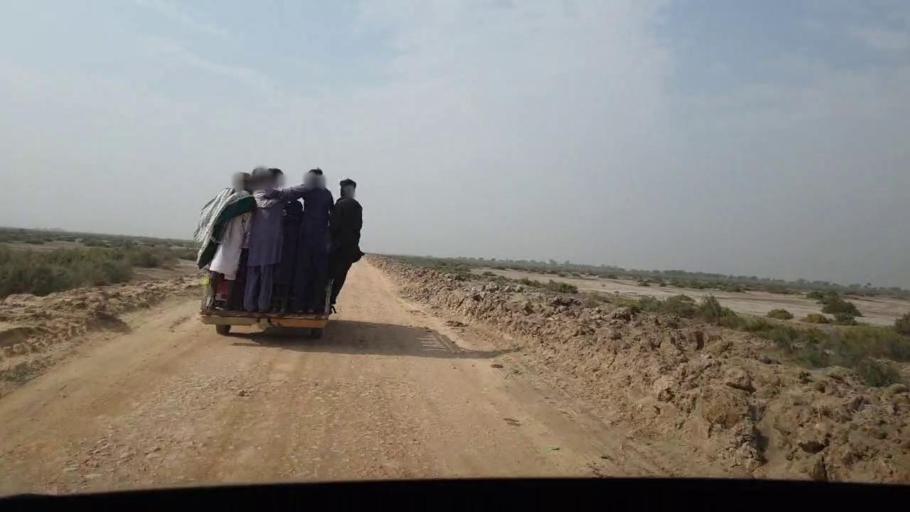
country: PK
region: Sindh
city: Chuhar Jamali
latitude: 24.3602
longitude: 67.9327
